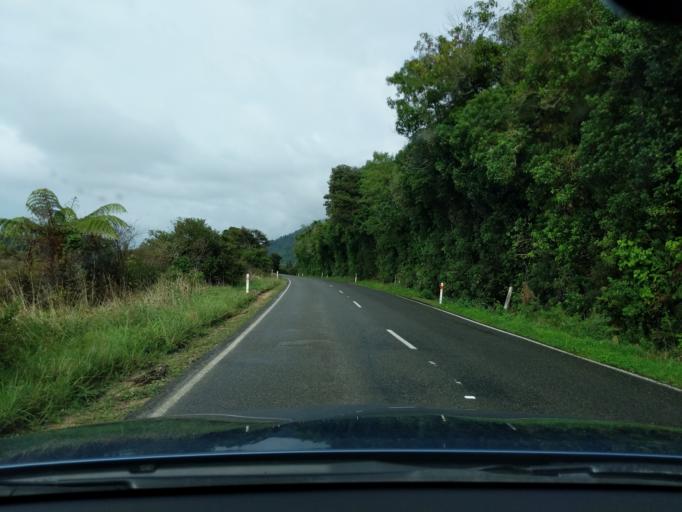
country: NZ
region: Tasman
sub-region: Tasman District
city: Takaka
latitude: -40.6531
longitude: 172.6525
